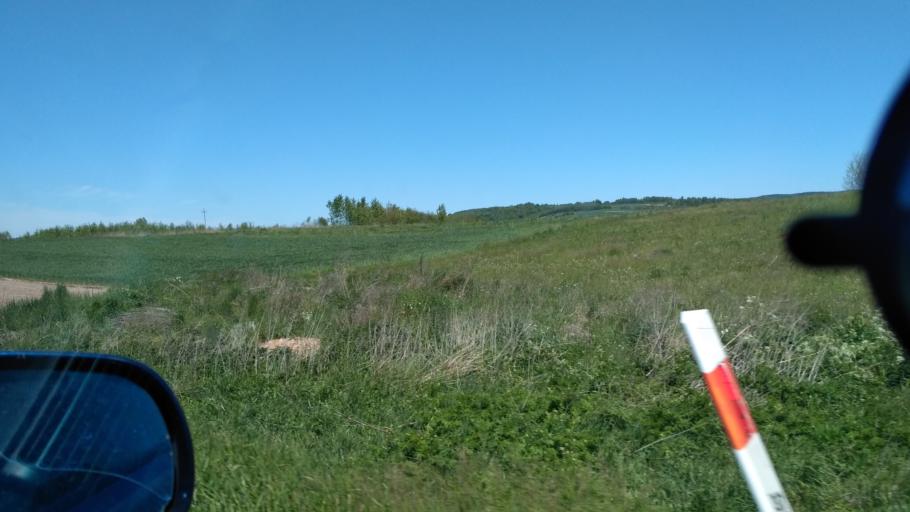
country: PL
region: Subcarpathian Voivodeship
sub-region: Powiat przemyski
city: Przedmiescie Dubieckie
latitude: 49.8267
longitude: 22.3161
